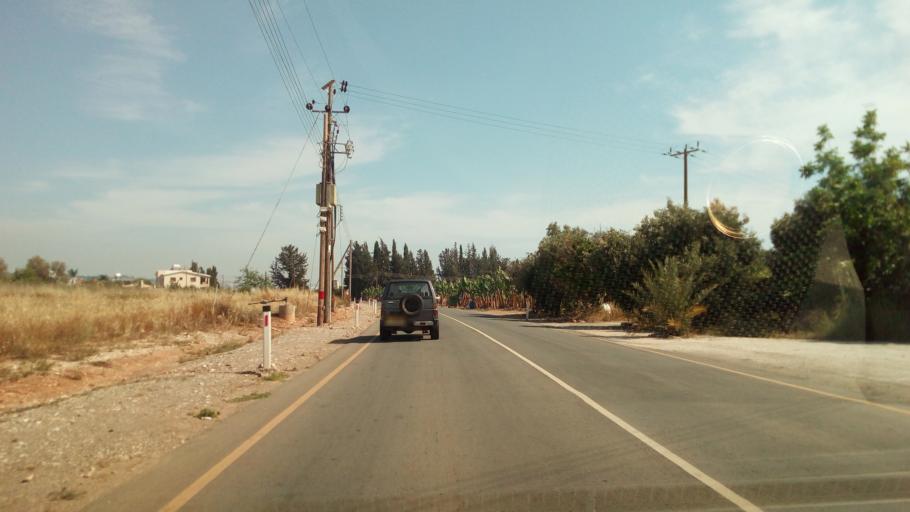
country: CY
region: Pafos
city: Pegeia
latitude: 34.8589
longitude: 32.3799
